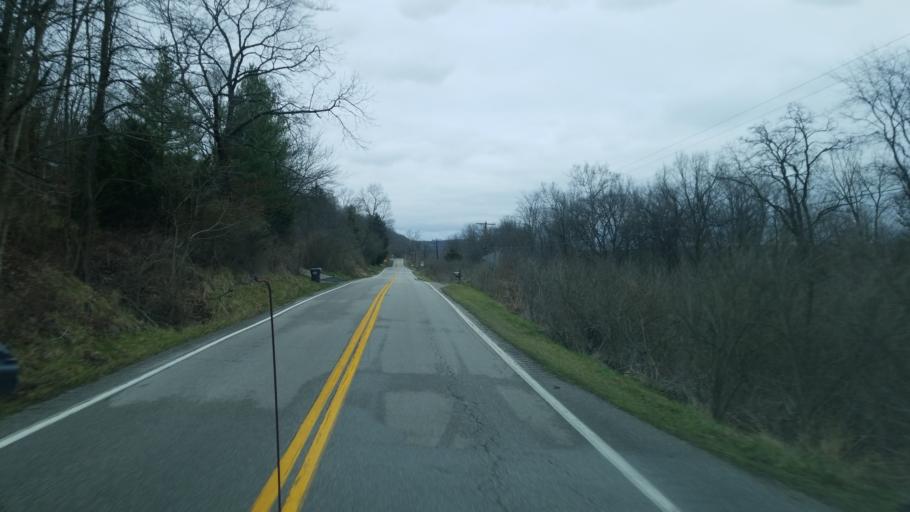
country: US
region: Ohio
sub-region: Clermont County
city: New Richmond
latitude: 38.9478
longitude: -84.2910
